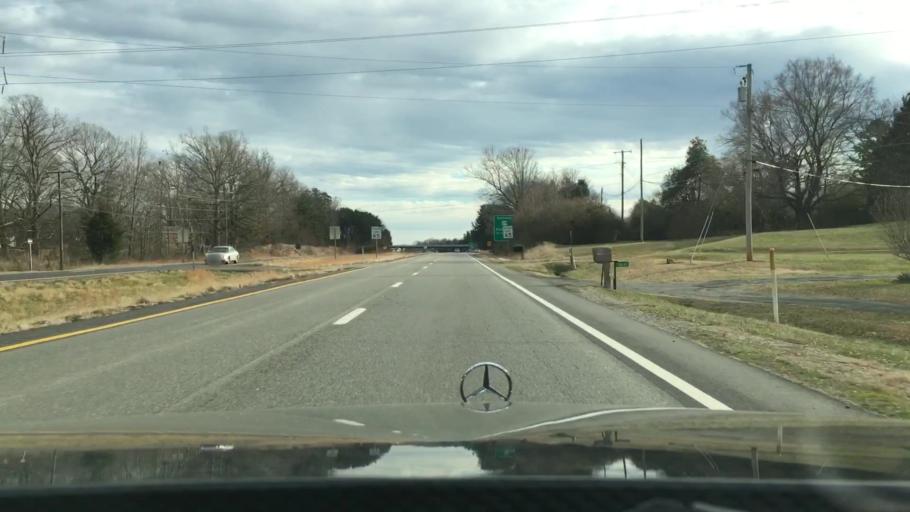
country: US
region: Virginia
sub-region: Pittsylvania County
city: Chatham
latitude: 36.8534
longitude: -79.3962
